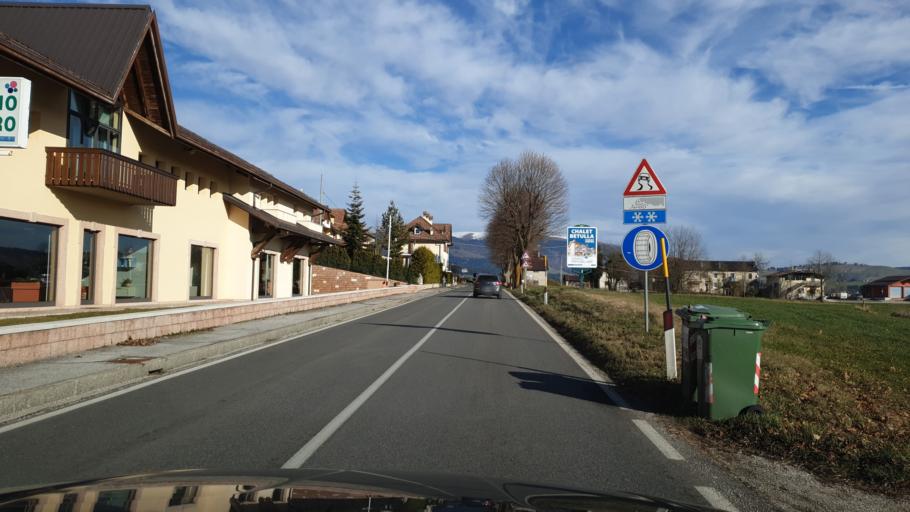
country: IT
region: Veneto
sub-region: Provincia di Vicenza
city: Canove di Roana
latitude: 45.8686
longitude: 11.4871
